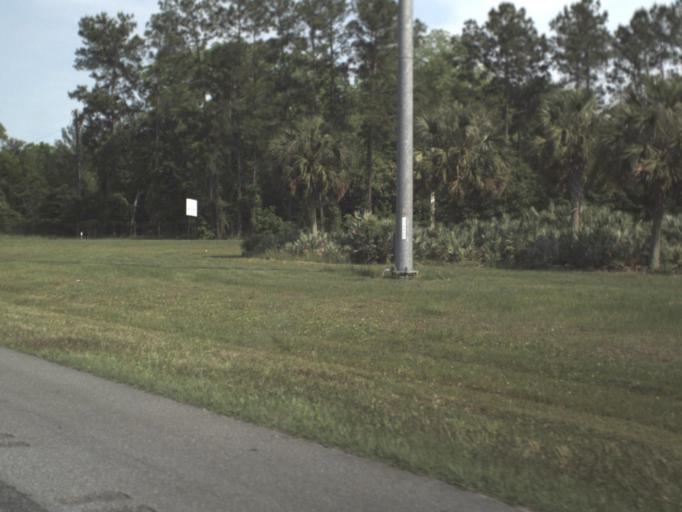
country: US
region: Florida
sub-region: Baker County
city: Macclenny
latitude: 30.2586
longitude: -82.1216
